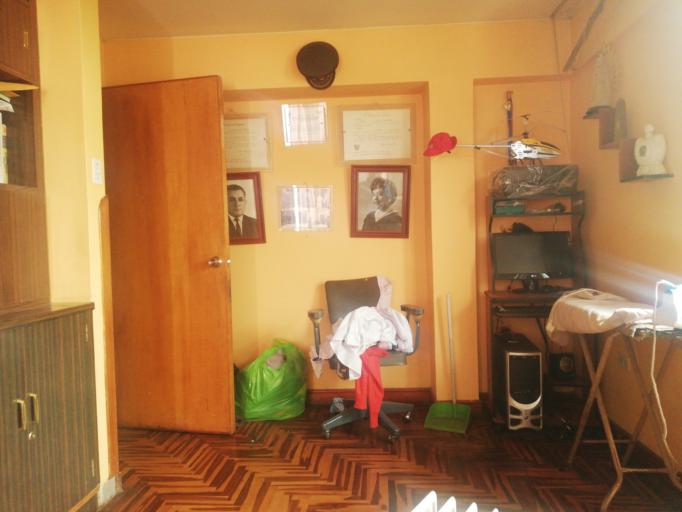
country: PE
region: Cusco
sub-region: Provincia de Cusco
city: Cusco
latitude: -13.5276
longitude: -71.9510
